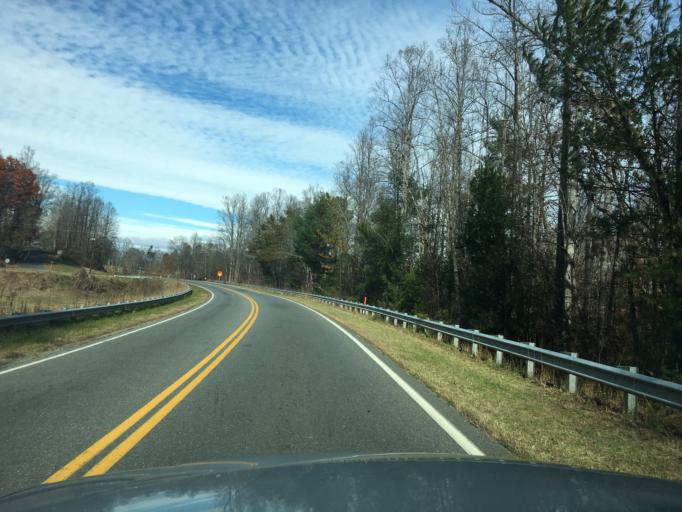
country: US
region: North Carolina
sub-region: McDowell County
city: Marion
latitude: 35.6574
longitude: -81.9744
